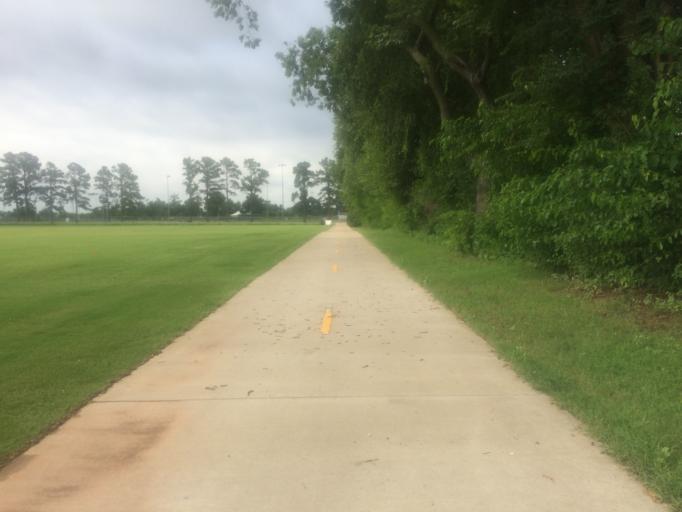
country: US
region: Oklahoma
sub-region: Cleveland County
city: Norman
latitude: 35.1981
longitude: -97.4402
